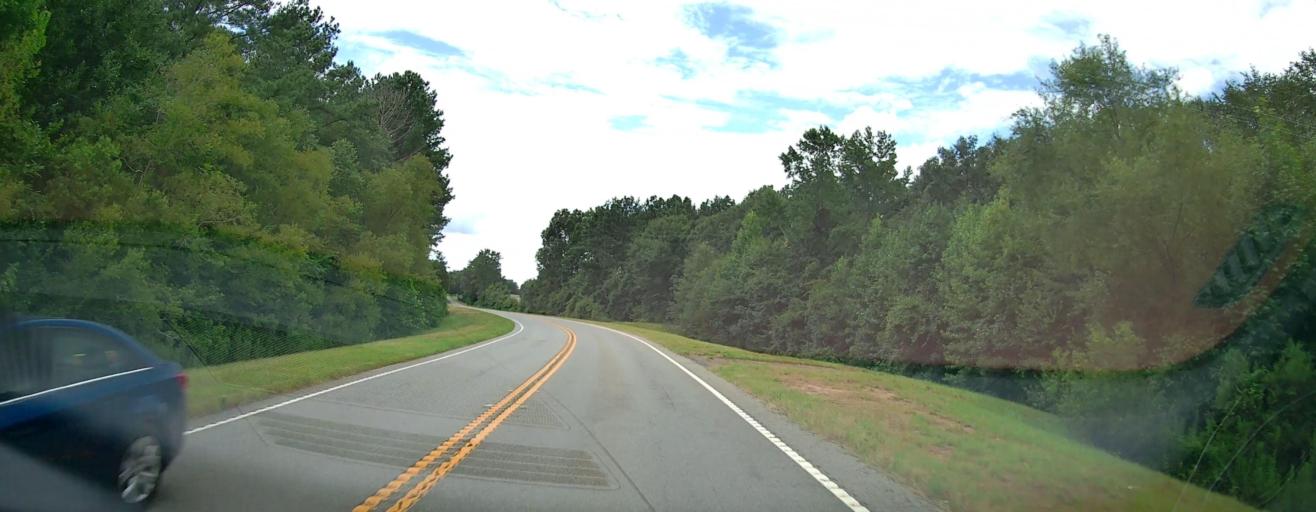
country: US
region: Georgia
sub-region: Macon County
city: Montezuma
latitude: 32.2939
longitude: -83.8939
